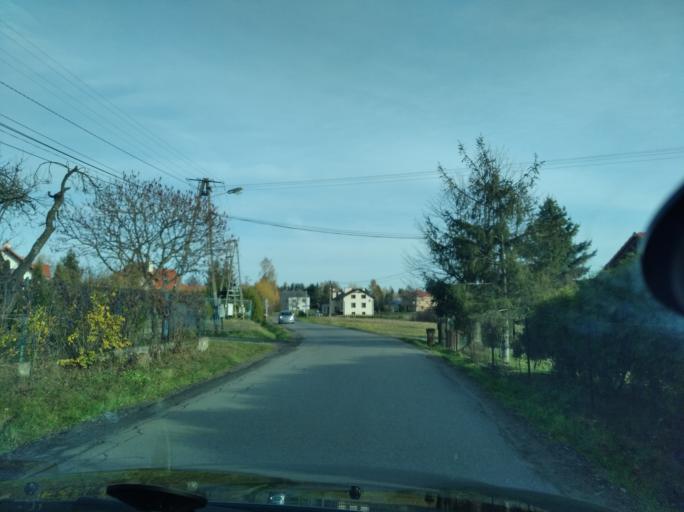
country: PL
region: Subcarpathian Voivodeship
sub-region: Powiat rzeszowski
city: Tyczyn
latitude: 50.0001
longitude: 22.0687
